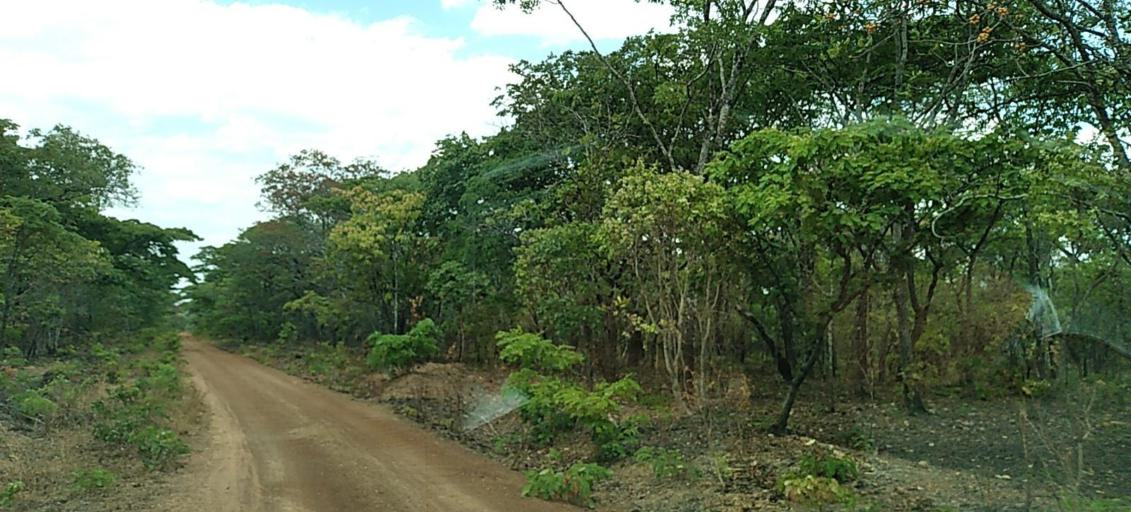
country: ZM
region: Copperbelt
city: Chililabombwe
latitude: -12.4610
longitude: 27.5956
